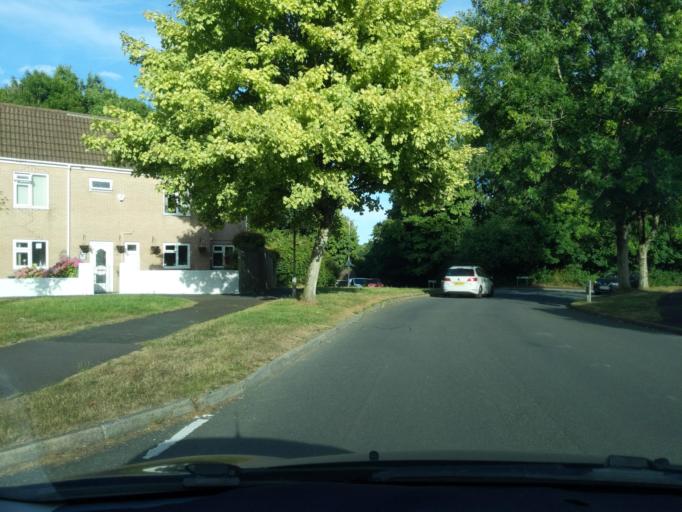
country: GB
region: England
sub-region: Plymouth
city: Plymstock
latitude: 50.3919
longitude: -4.1007
